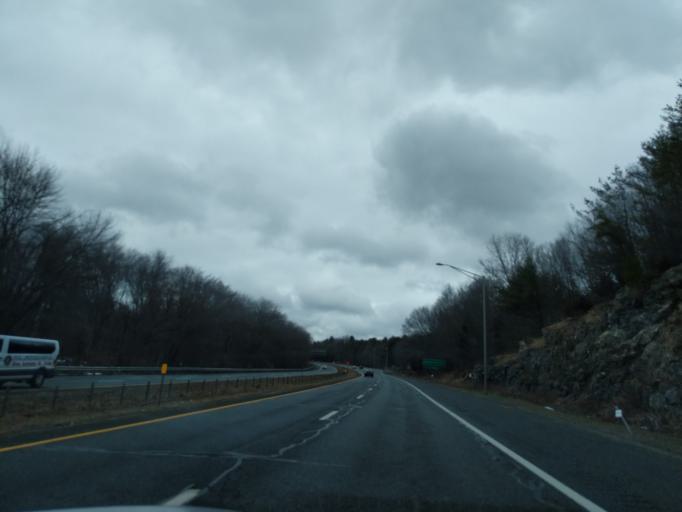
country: US
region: Massachusetts
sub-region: Worcester County
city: Blackstone
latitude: 42.0039
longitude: -71.5626
